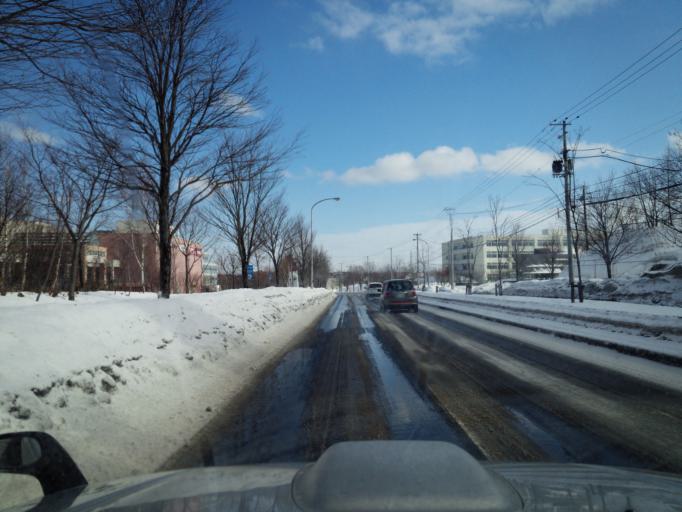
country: JP
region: Hokkaido
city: Kitahiroshima
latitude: 42.9963
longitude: 141.4592
